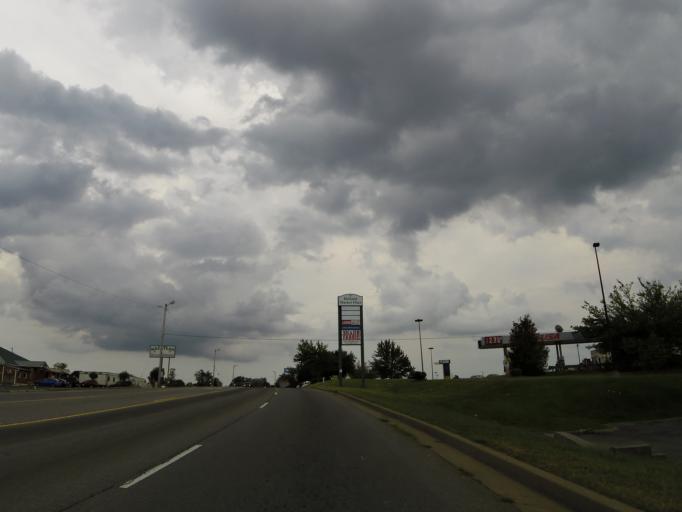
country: US
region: Tennessee
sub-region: Dickson County
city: Dickson
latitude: 36.0622
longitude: -87.3818
